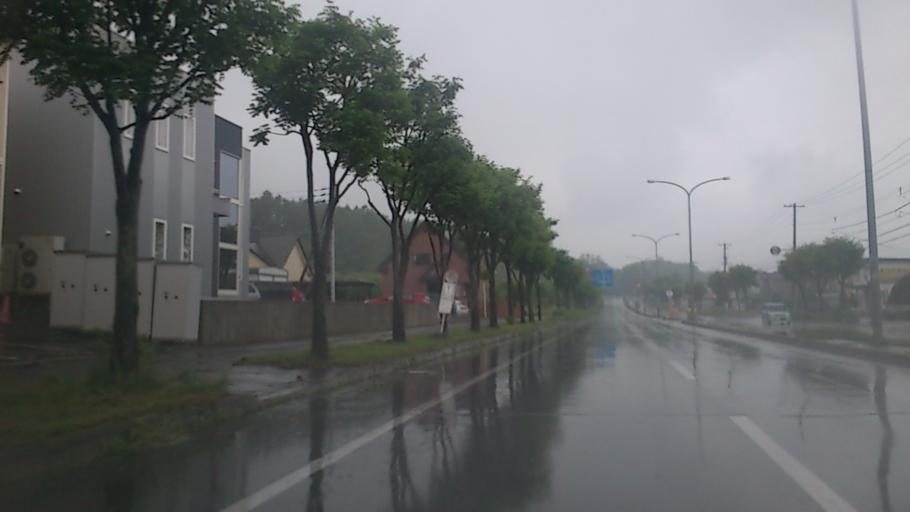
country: JP
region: Hokkaido
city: Obihiro
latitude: 42.9031
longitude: 143.1525
